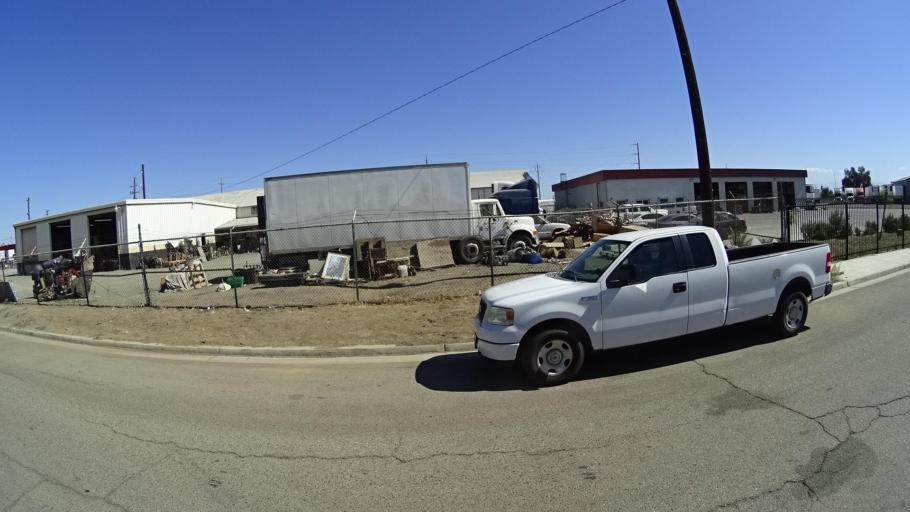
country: US
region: California
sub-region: Fresno County
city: Fresno
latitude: 36.7128
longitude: -119.7774
